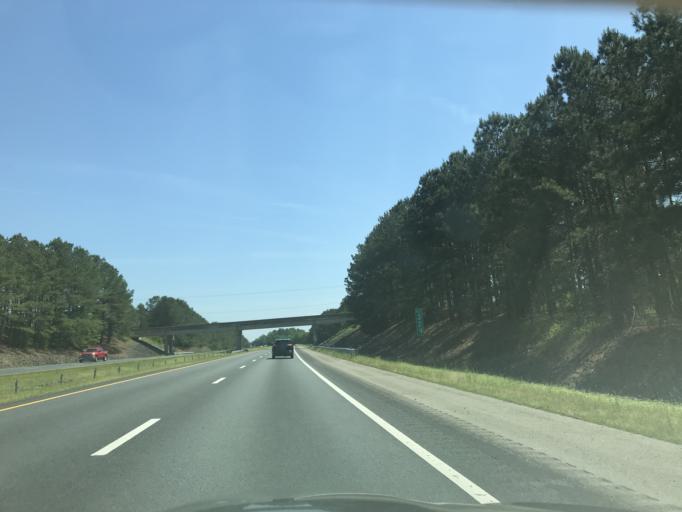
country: US
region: North Carolina
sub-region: Johnston County
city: Benson
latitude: 35.3770
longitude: -78.5051
